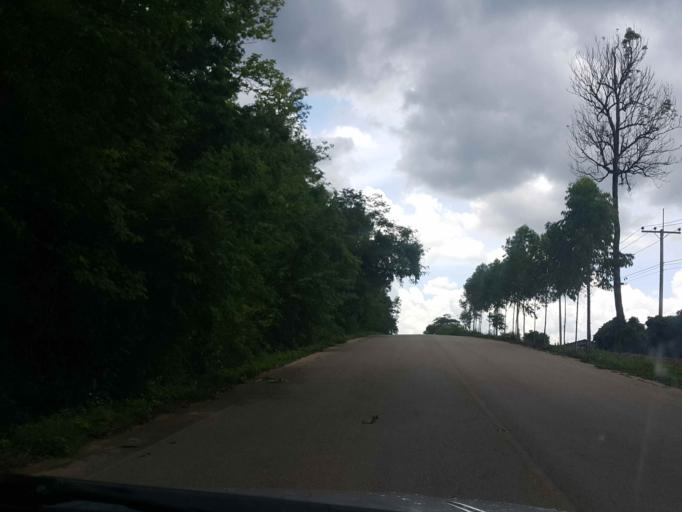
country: TH
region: Phayao
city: Dok Kham Tai
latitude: 18.9785
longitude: 100.0705
